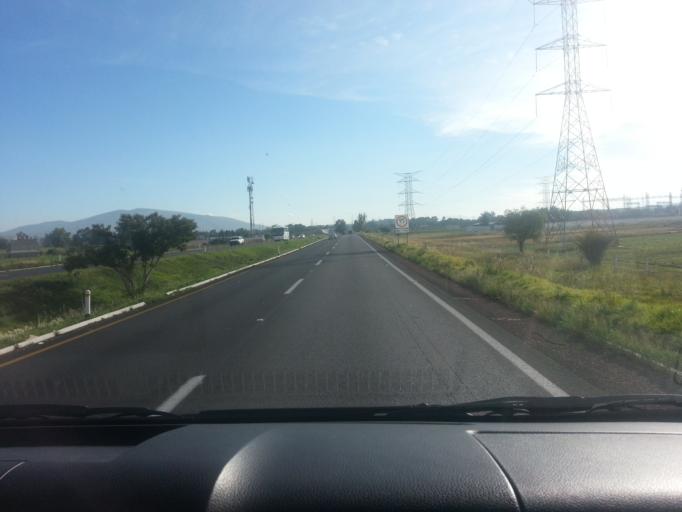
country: MX
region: Morelos
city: Xometla
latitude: 19.6442
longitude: -98.8933
